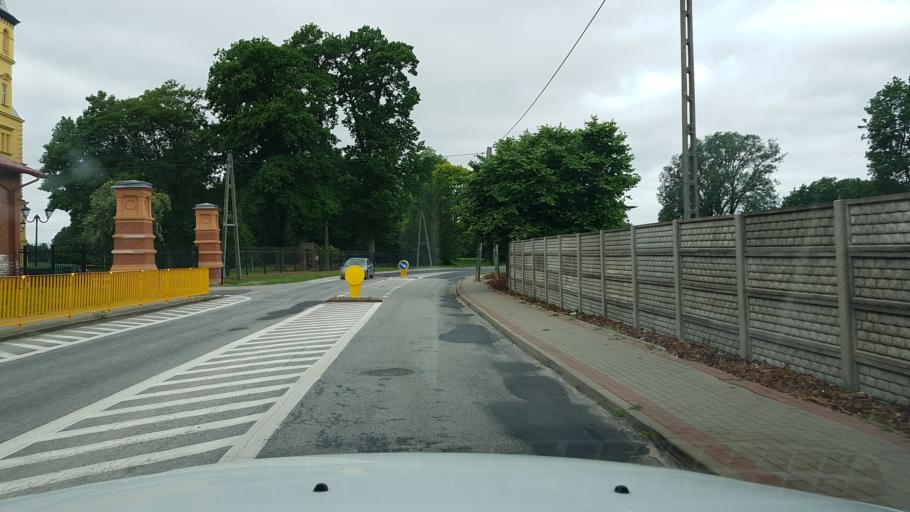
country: PL
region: West Pomeranian Voivodeship
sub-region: Powiat kamienski
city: Swierzno
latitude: 53.9497
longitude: 15.0078
